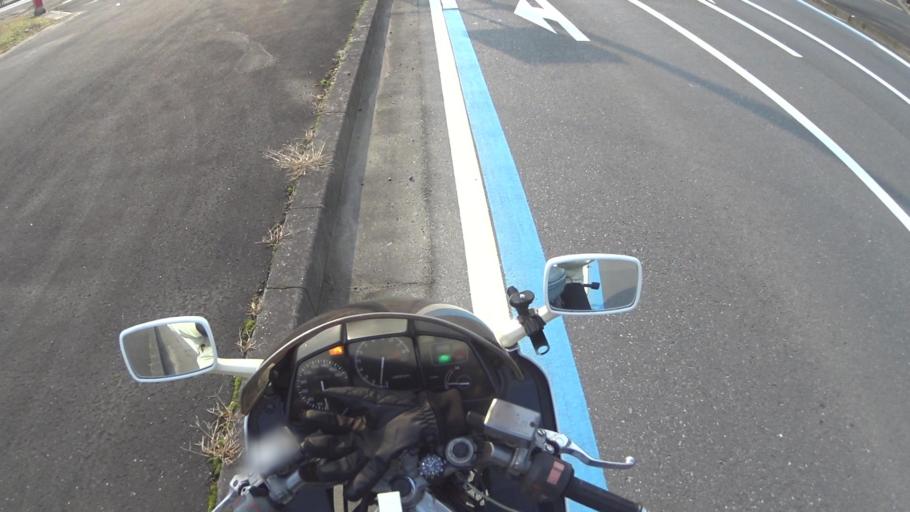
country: JP
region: Kyoto
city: Fukuchiyama
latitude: 35.2993
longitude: 135.1796
